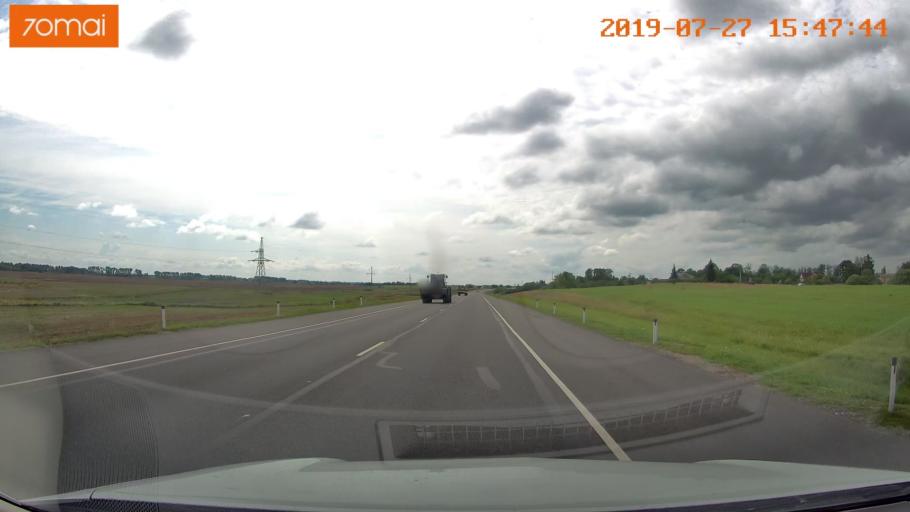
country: RU
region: Kaliningrad
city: Gusev
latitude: 54.5997
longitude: 22.0802
